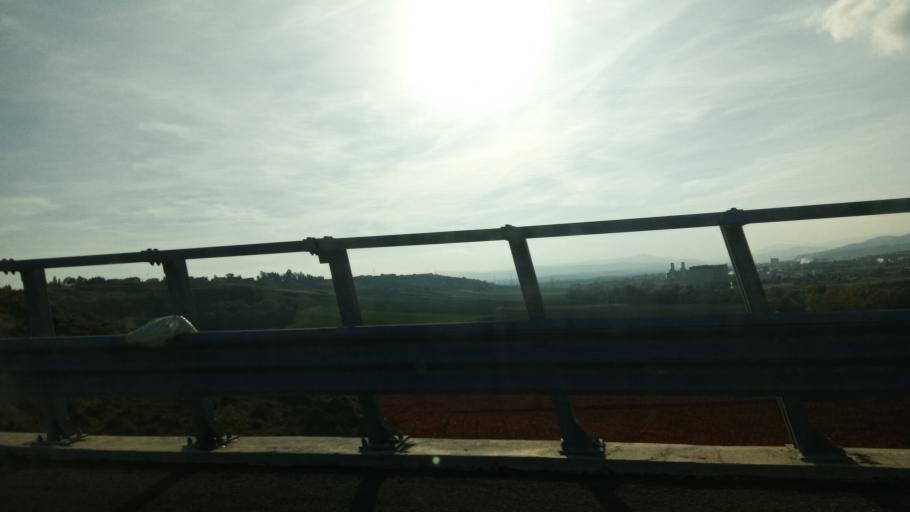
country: IT
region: Molise
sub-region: Provincia di Campobasso
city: Campomarino
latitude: 41.9527
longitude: 15.0177
